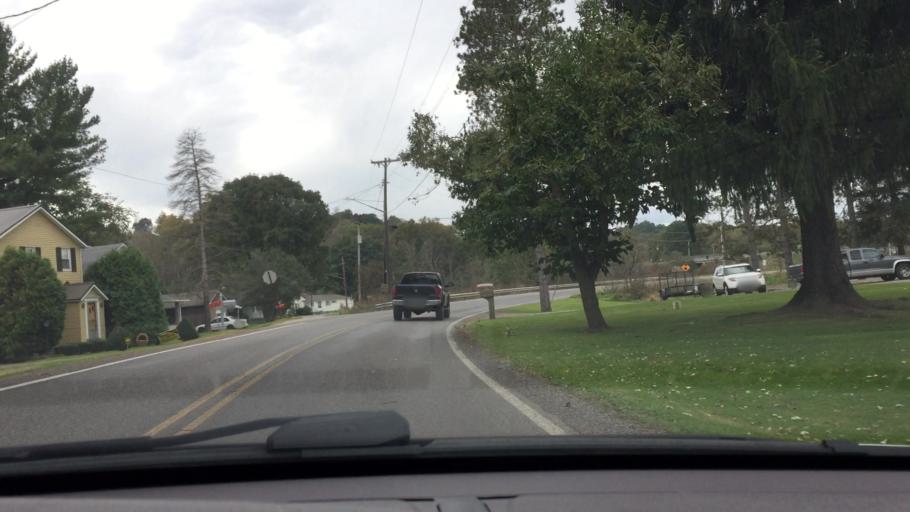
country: US
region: Pennsylvania
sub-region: Lawrence County
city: Oakwood
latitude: 41.0142
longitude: -80.4397
